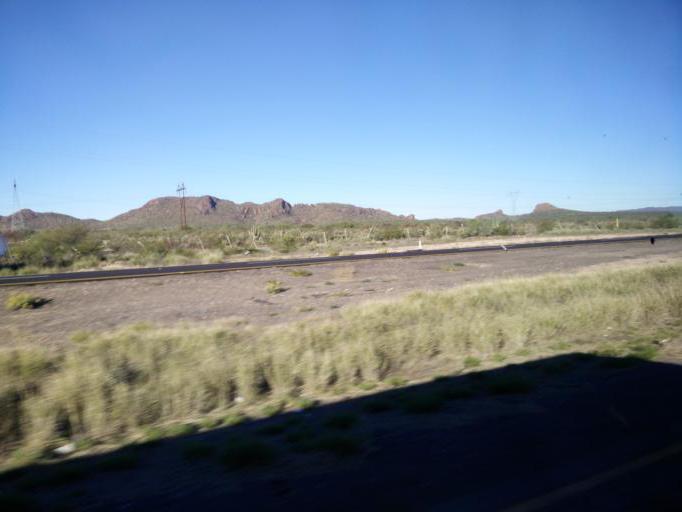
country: MX
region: Sonora
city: Heroica Guaymas
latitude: 28.2755
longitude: -111.0375
